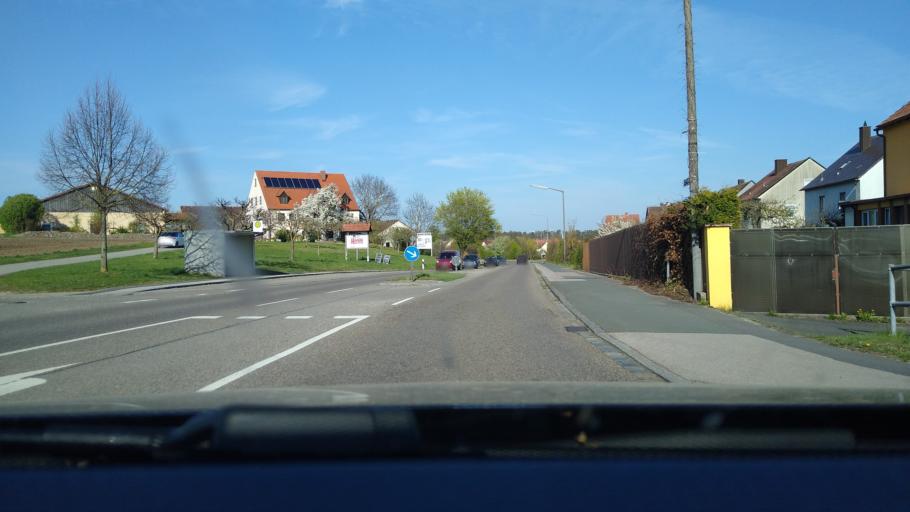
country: DE
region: Bavaria
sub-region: Regierungsbezirk Mittelfranken
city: Kammerstein
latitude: 49.3026
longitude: 10.9880
